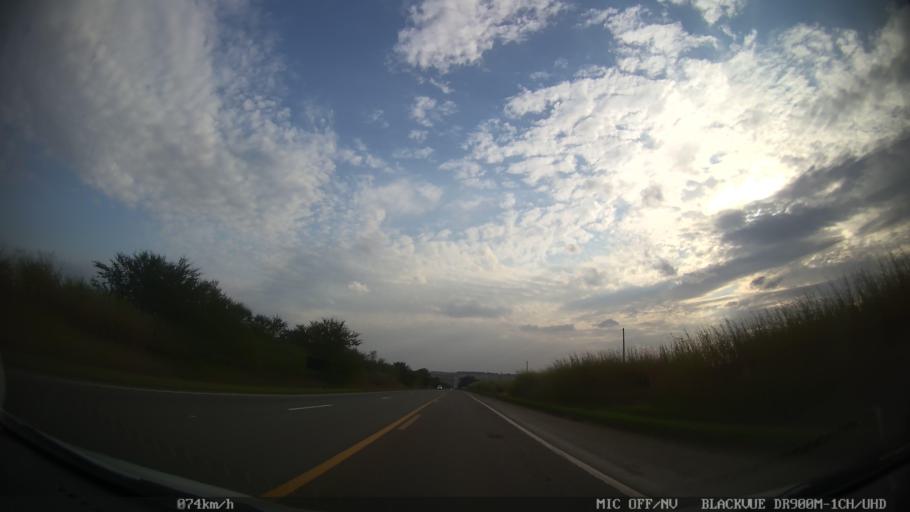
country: BR
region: Sao Paulo
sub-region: Cosmopolis
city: Cosmopolis
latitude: -22.6271
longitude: -47.2668
